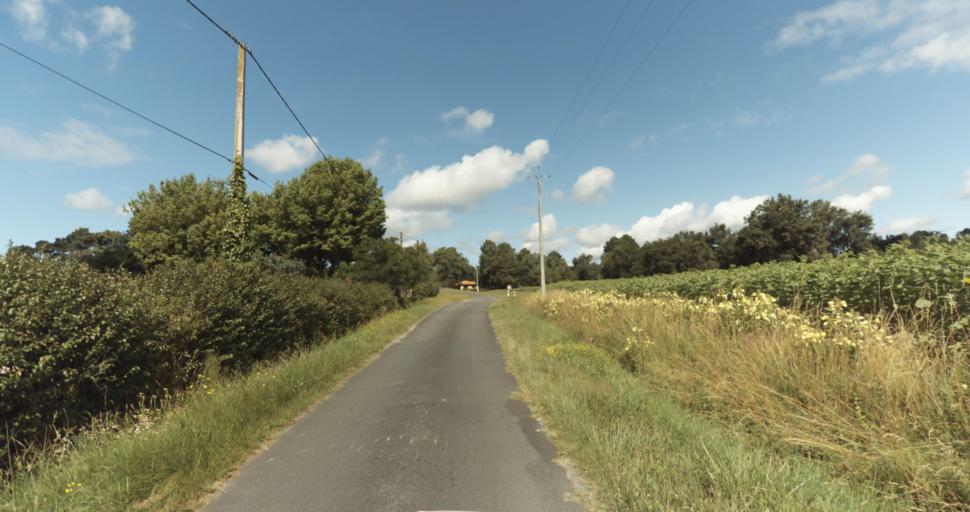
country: FR
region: Aquitaine
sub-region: Departement de la Gironde
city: Bazas
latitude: 44.4636
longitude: -0.2198
